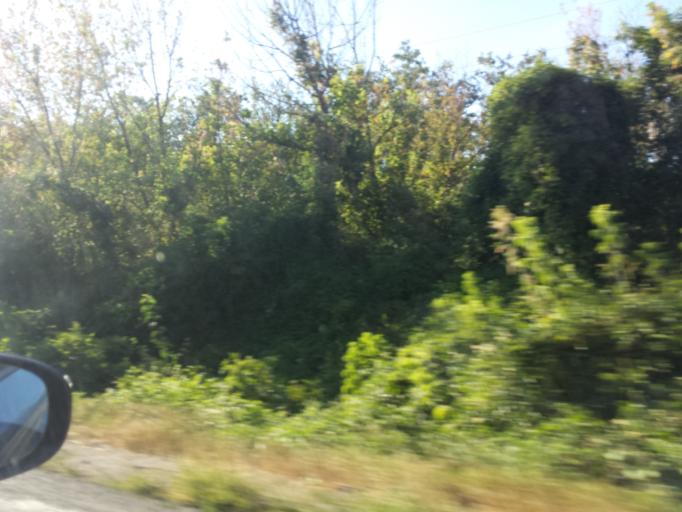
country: RO
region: Ialomita
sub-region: Comuna Cosambesti
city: Cosambesti
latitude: 44.5764
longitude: 27.4042
